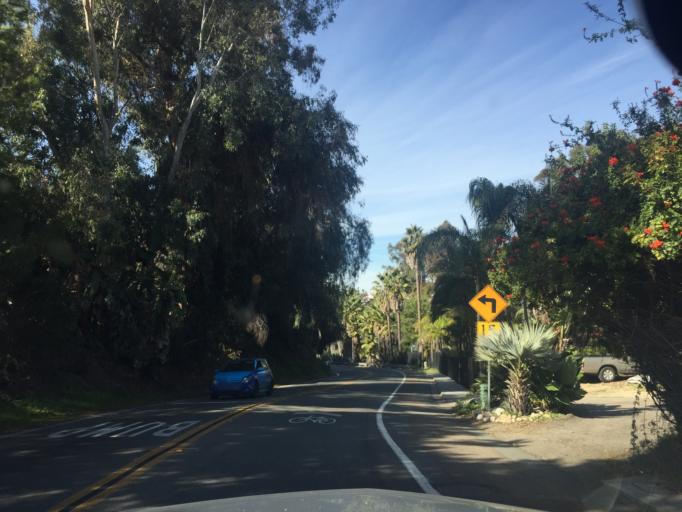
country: US
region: California
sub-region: San Diego County
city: Lemon Grove
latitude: 32.7592
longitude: -117.0938
